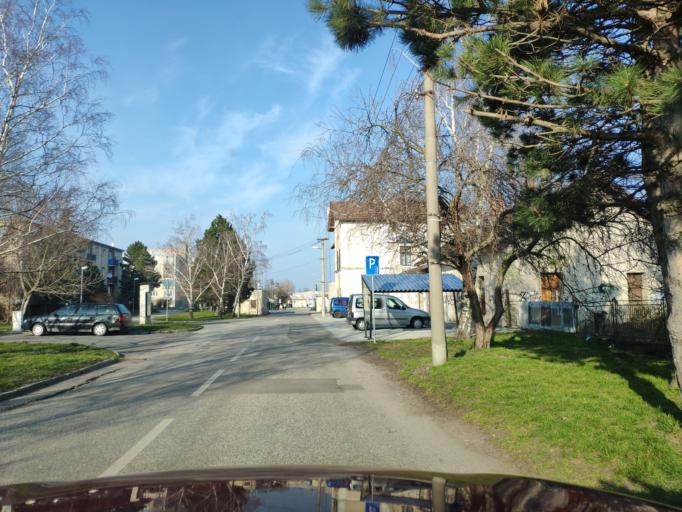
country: SK
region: Bratislavsky
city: Svaty Jur
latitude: 48.2473
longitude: 17.2166
